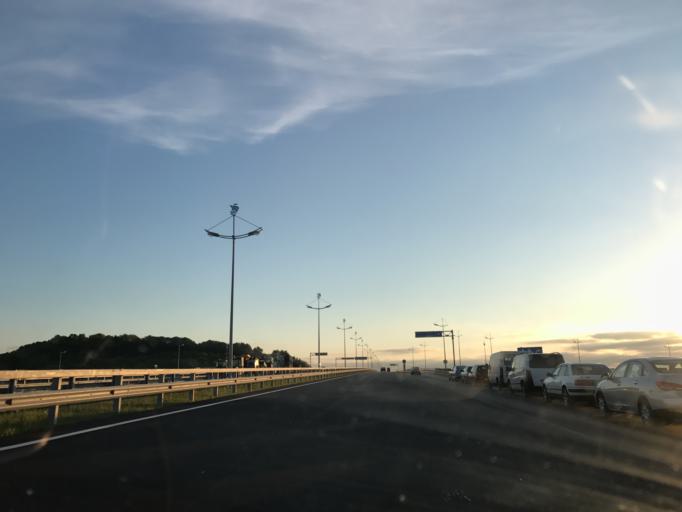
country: RU
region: Kaliningrad
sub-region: Gorod Kaliningrad
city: Pionerskiy
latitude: 54.9203
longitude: 20.2734
